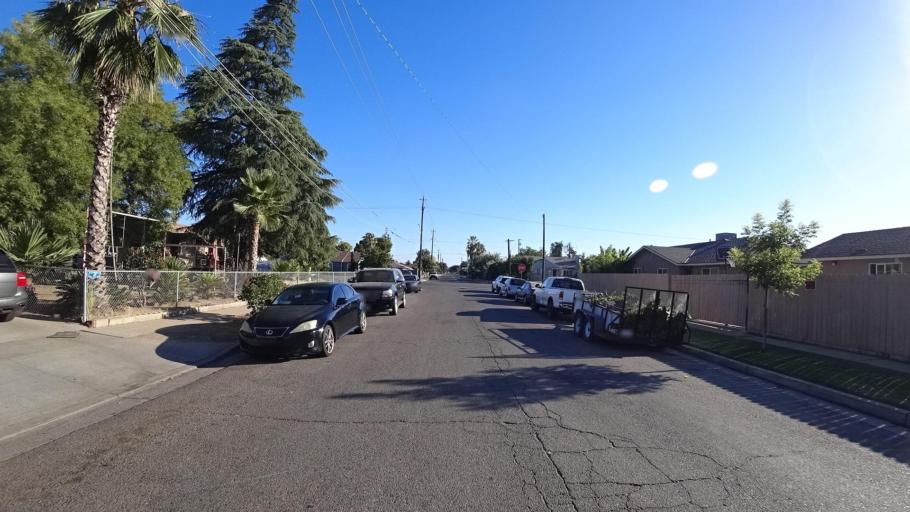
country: US
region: California
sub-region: Fresno County
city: Fresno
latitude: 36.7716
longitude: -119.8222
